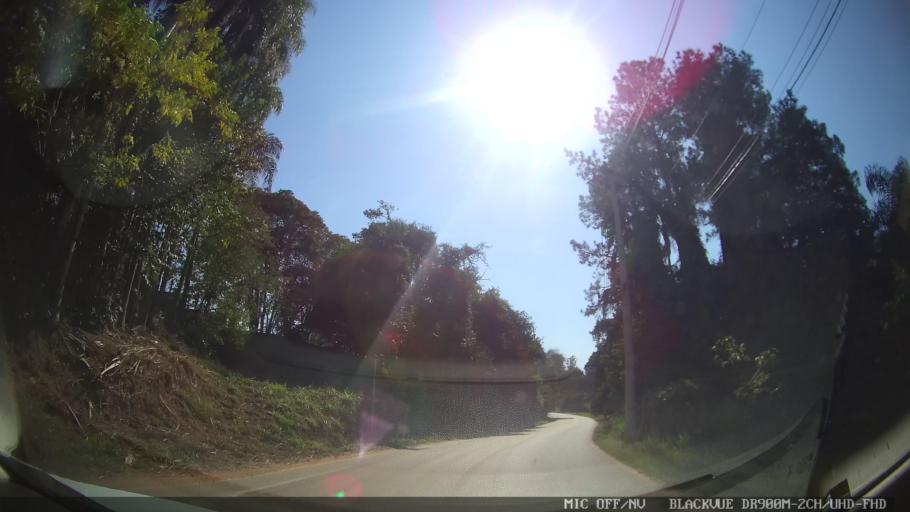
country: BR
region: Sao Paulo
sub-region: Itupeva
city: Itupeva
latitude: -23.1241
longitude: -47.0455
